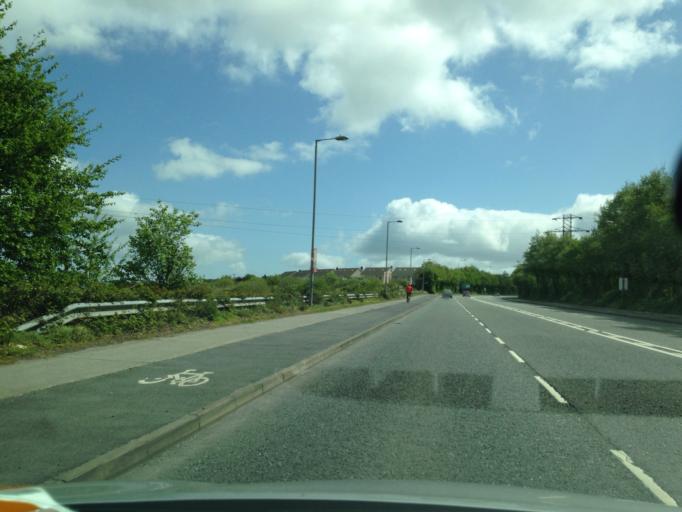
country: IE
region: Connaught
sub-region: County Galway
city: Gaillimh
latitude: 53.2918
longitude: -9.0272
